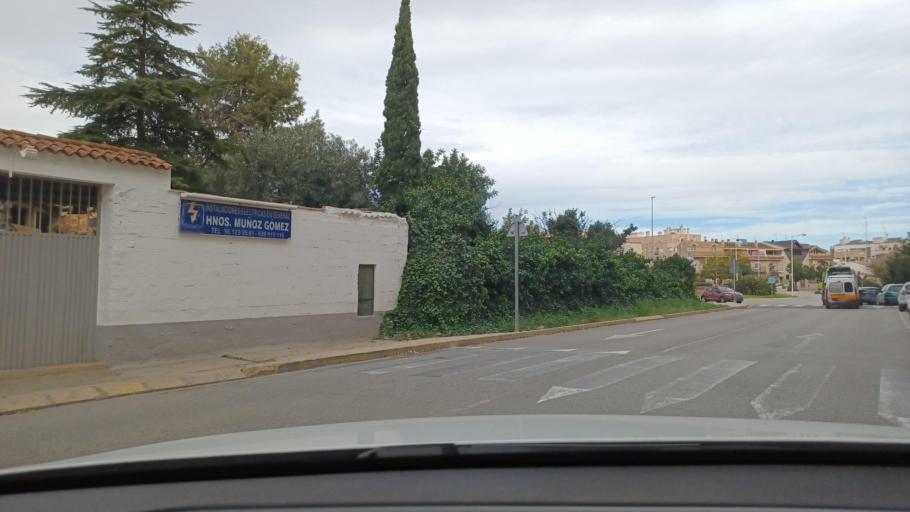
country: ES
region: Valencia
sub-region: Provincia de Valencia
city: Picassent
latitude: 39.3664
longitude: -0.4612
